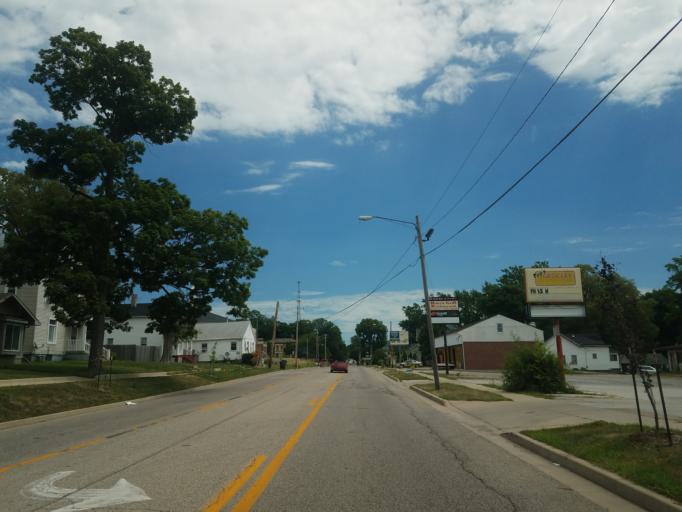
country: US
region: Illinois
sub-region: McLean County
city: Bloomington
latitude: 40.4821
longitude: -89.0046
